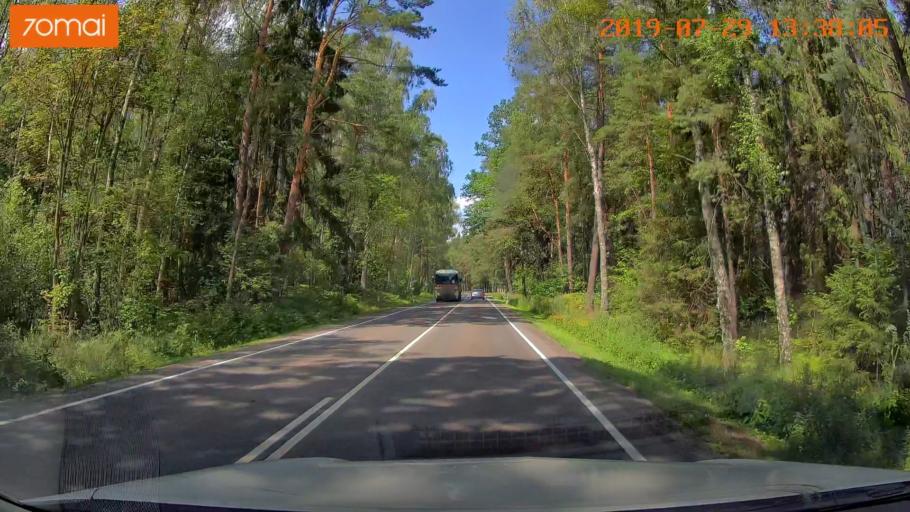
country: RU
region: Kaliningrad
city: Volochayevskoye
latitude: 54.7186
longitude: 20.1756
